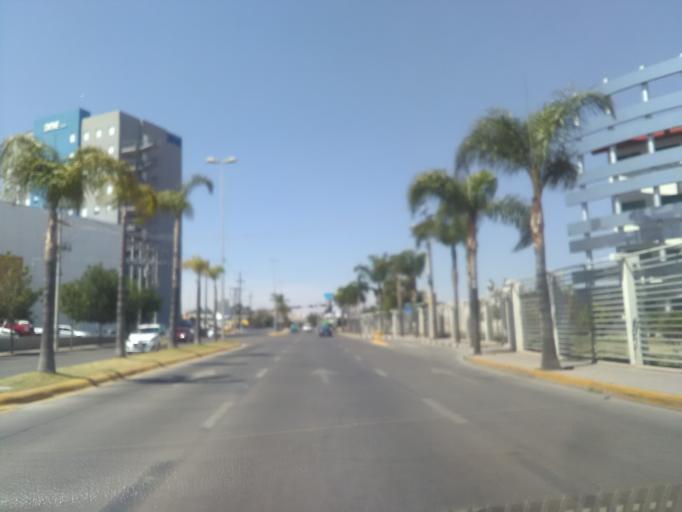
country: MX
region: Durango
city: Victoria de Durango
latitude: 24.0355
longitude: -104.6490
